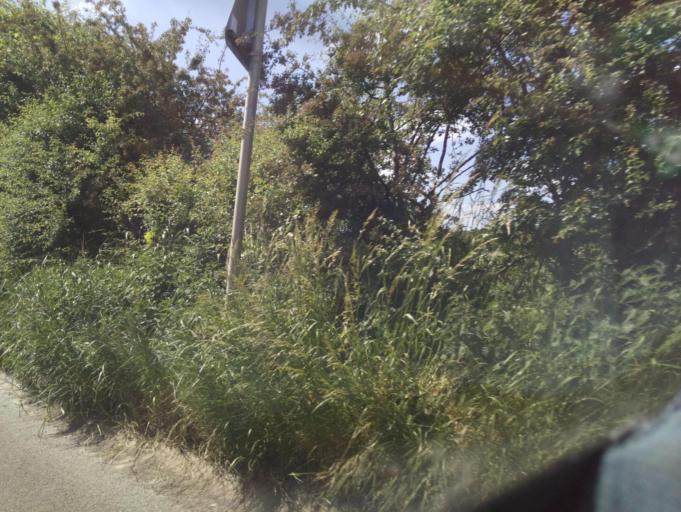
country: GB
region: England
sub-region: Wiltshire
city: Devizes
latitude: 51.3667
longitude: -1.9632
